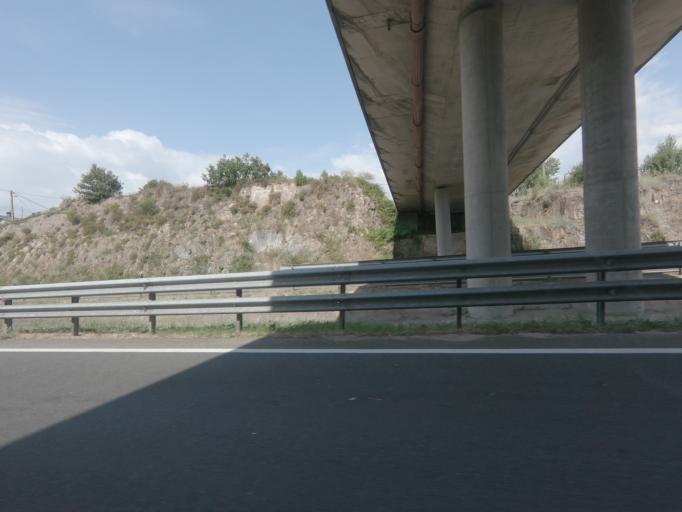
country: ES
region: Galicia
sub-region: Provincia de Ourense
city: Ourense
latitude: 42.3243
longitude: -7.8876
